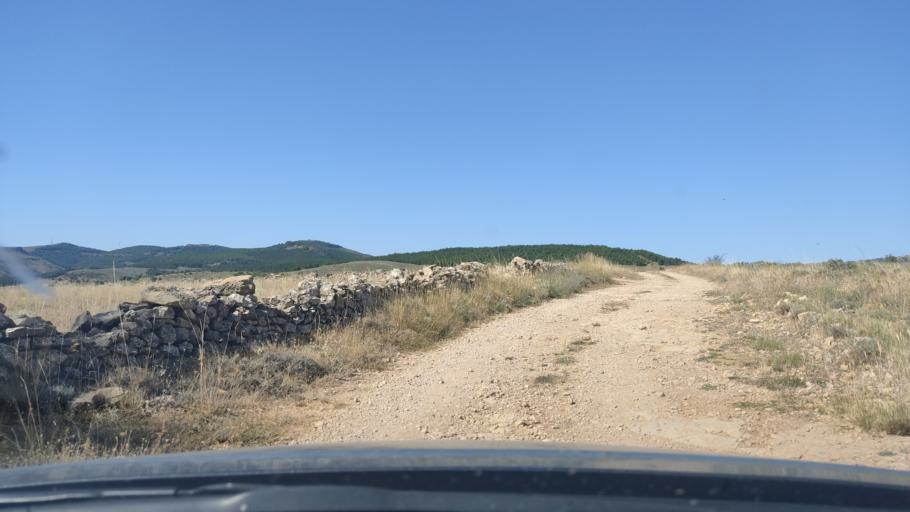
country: ES
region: Aragon
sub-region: Provincia de Teruel
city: Monforte de Moyuela
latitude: 41.0509
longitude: -1.0282
